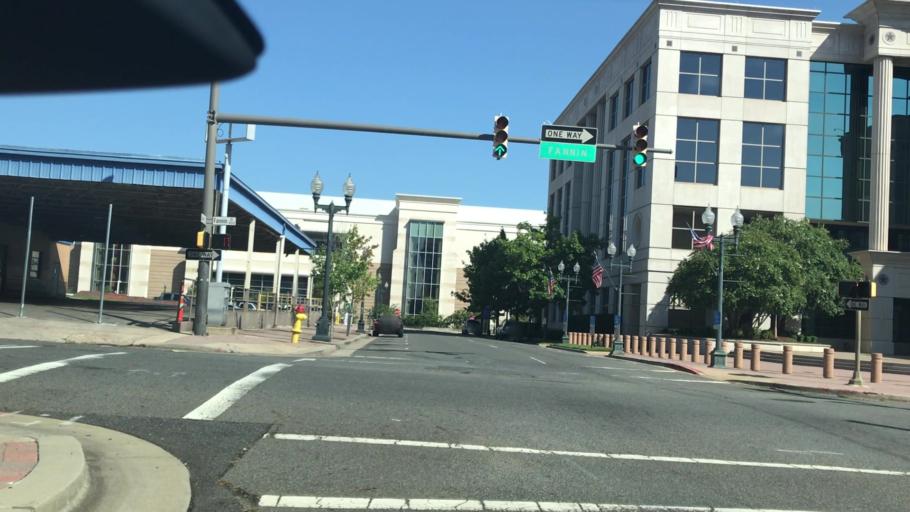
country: US
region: Louisiana
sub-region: Caddo Parish
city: Shreveport
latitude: 32.5152
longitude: -93.7505
